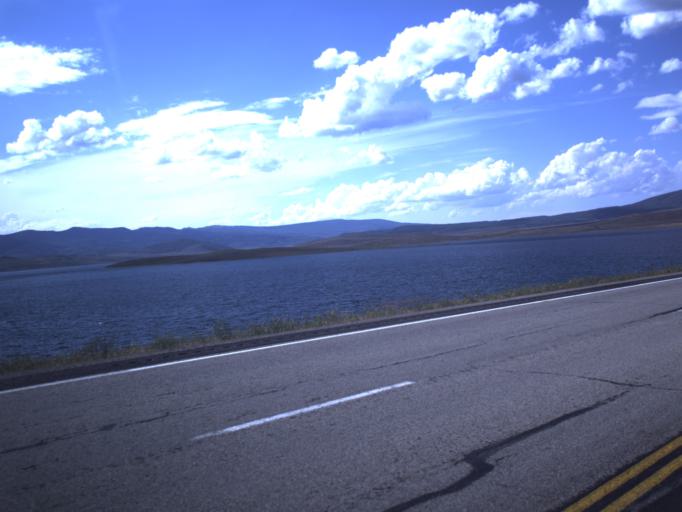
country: US
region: Utah
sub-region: Wasatch County
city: Heber
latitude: 40.2007
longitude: -111.1048
